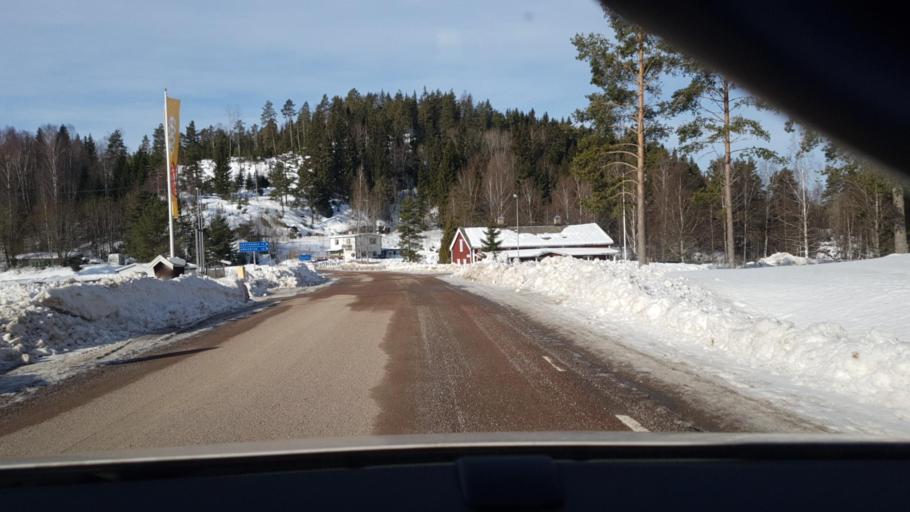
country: NO
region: Hedmark
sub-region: Eidskog
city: Skotterud
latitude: 59.8175
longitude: 12.0118
